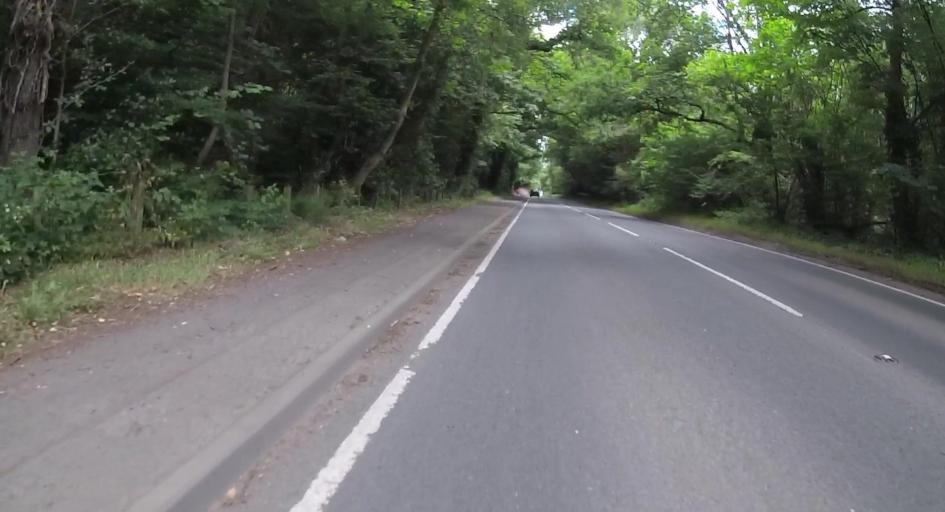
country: GB
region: England
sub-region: Hampshire
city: Fleet
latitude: 51.2546
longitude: -0.8253
